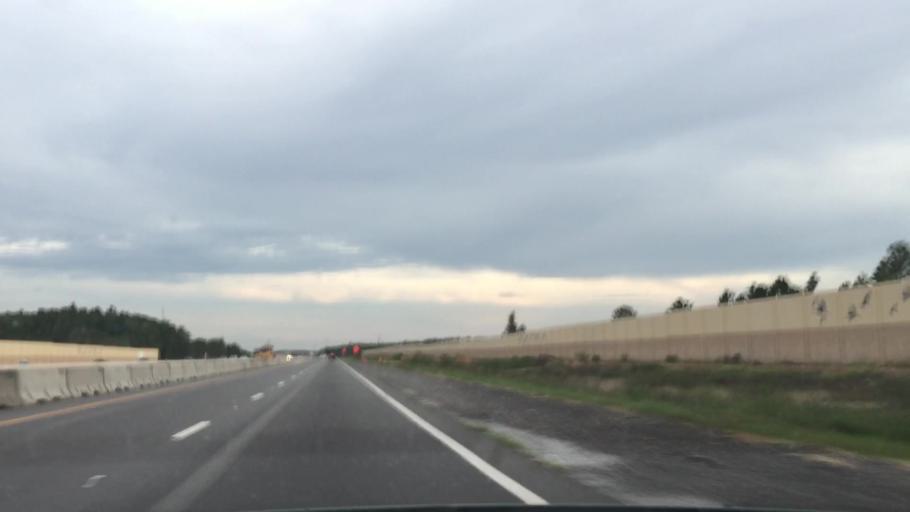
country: US
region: Florida
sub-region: Orange County
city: Southchase
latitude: 28.3886
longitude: -81.3916
